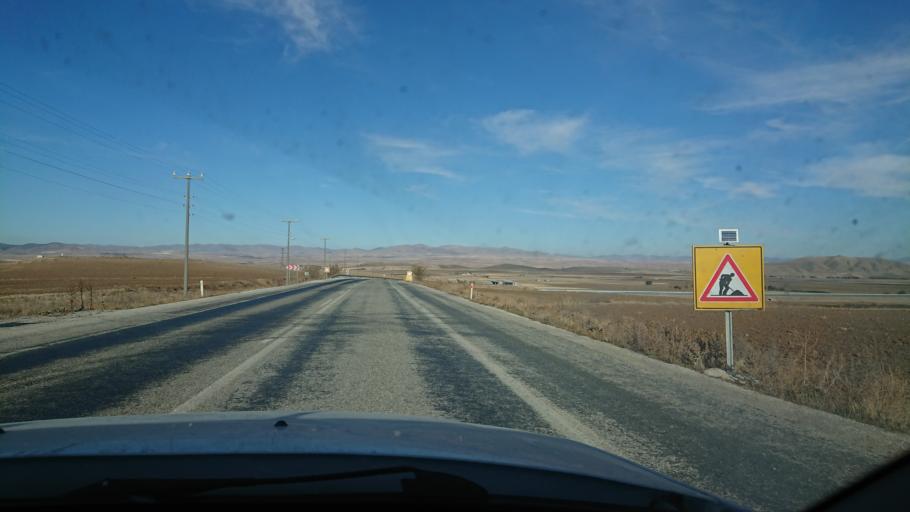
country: TR
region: Aksaray
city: Sariyahsi
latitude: 38.9953
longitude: 33.8498
